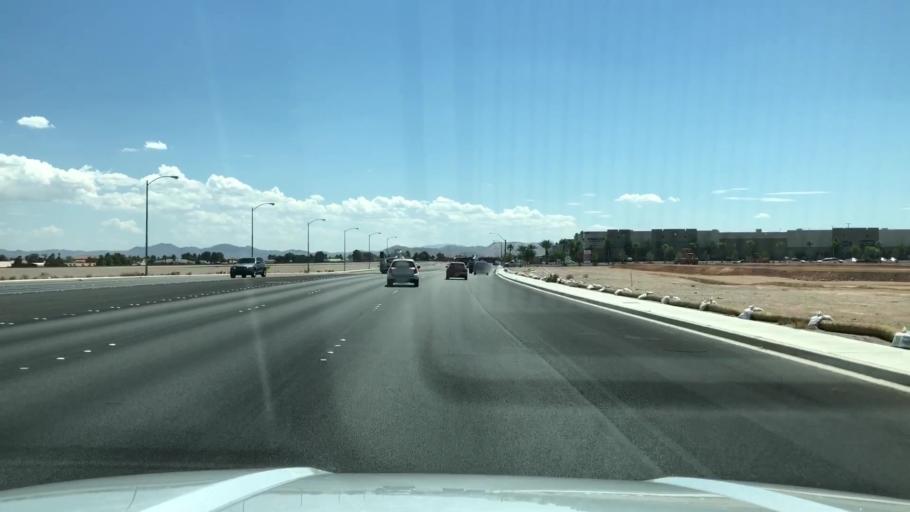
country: US
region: Nevada
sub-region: Clark County
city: Enterprise
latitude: 36.0658
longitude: -115.2080
